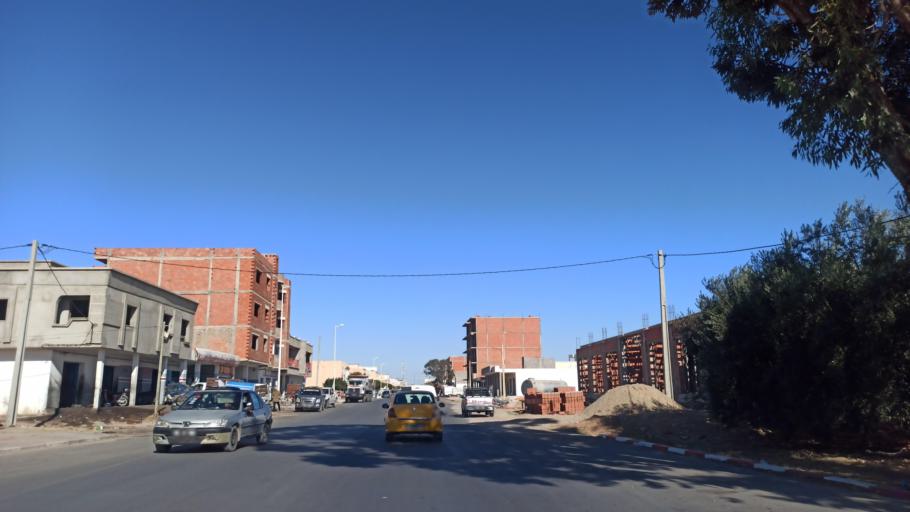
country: TN
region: Sidi Bu Zayd
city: Bi'r al Hufayy
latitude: 34.9199
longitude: 9.1872
